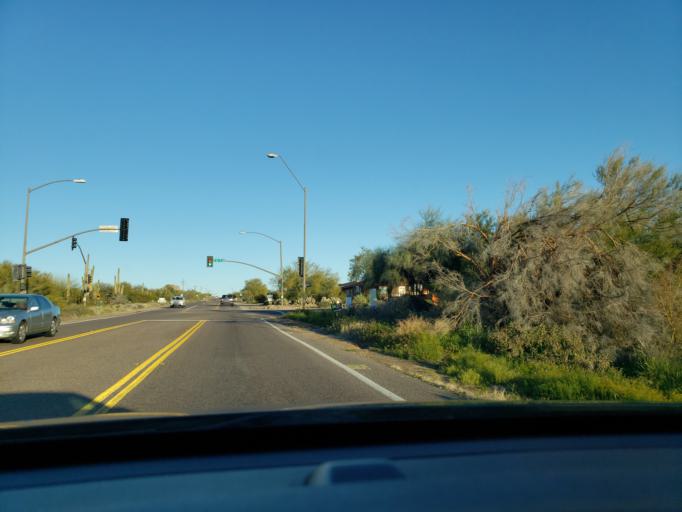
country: US
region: Arizona
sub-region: Maricopa County
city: Cave Creek
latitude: 33.7991
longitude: -111.9526
